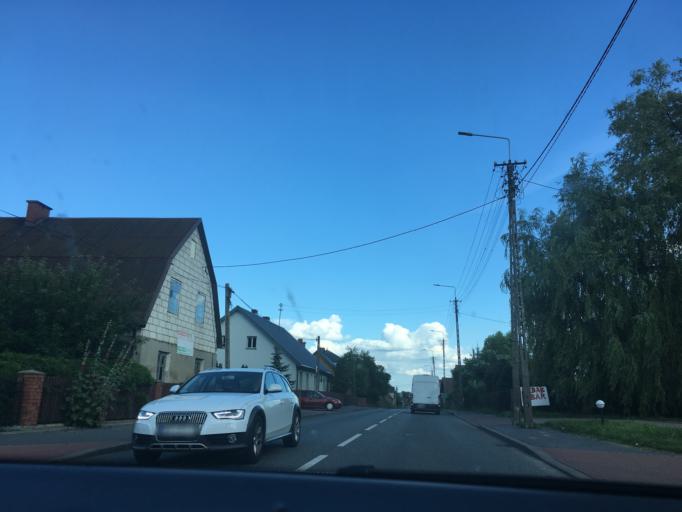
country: PL
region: Podlasie
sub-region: Powiat bialostocki
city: Zabludow
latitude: 53.0183
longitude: 23.3282
